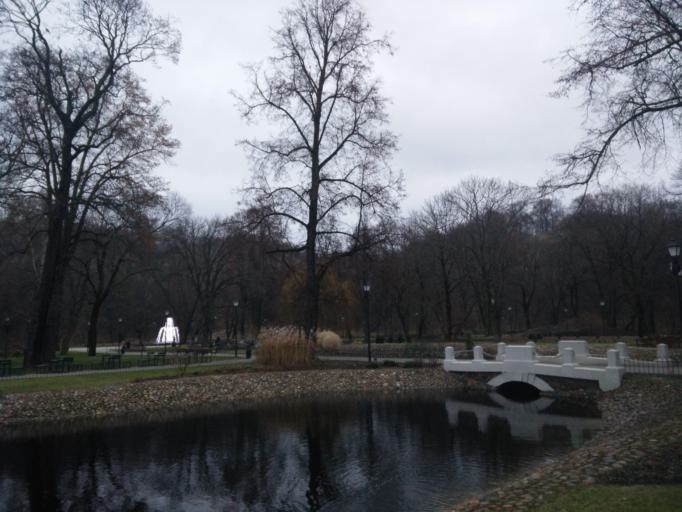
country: LT
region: Vilnius County
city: Rasos
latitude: 54.6827
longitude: 25.2964
